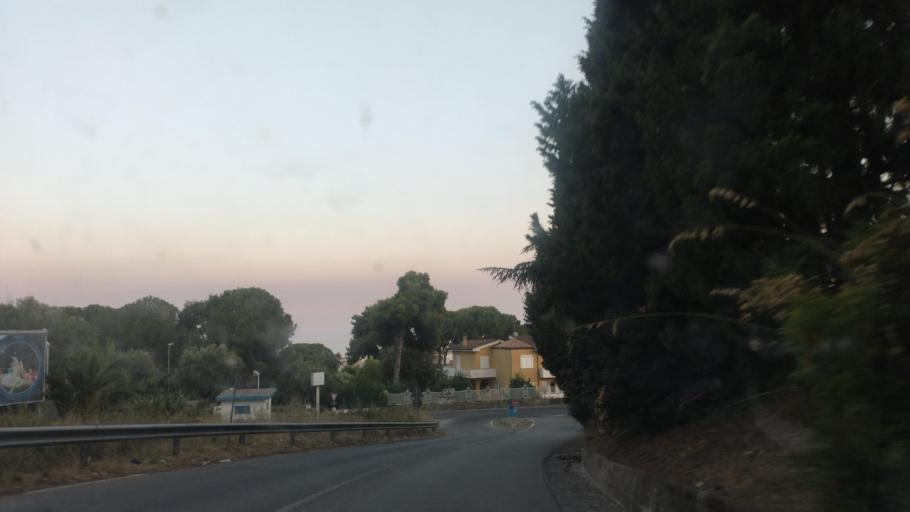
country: IT
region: Calabria
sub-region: Provincia di Catanzaro
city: Montepaone Lido
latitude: 38.7436
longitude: 16.5524
